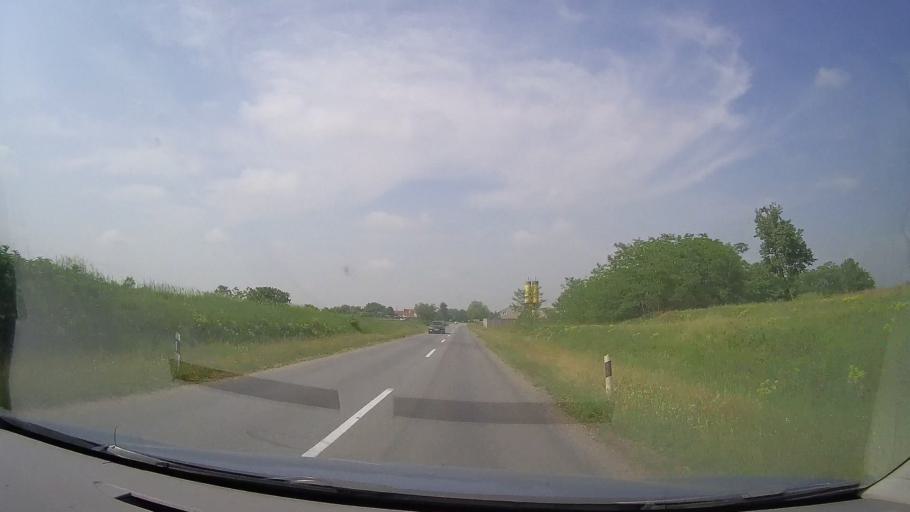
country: RS
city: Padina
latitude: 45.1341
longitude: 20.7339
